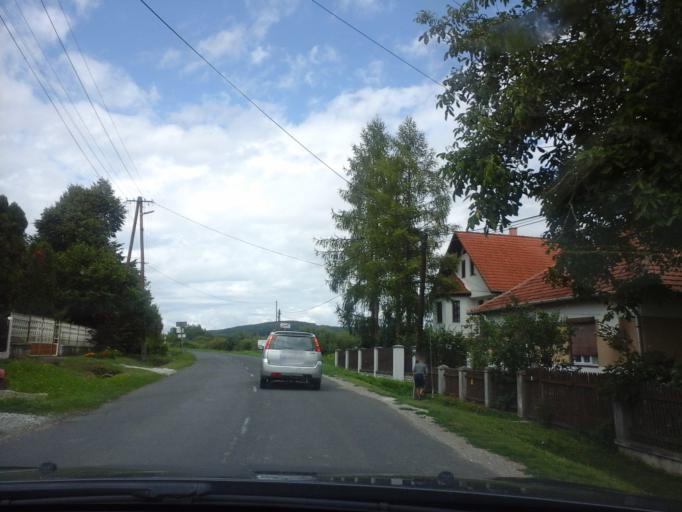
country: HU
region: Borsod-Abauj-Zemplen
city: Rudabanya
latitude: 48.3814
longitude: 20.5671
